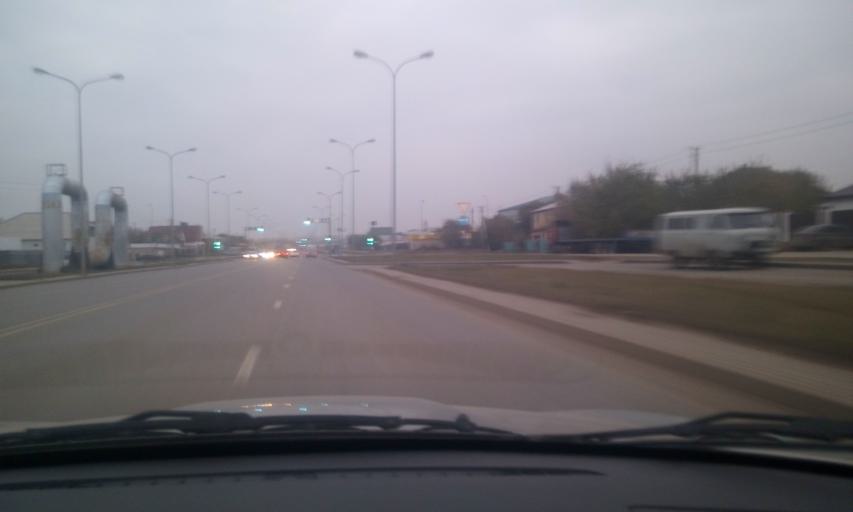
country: KZ
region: Astana Qalasy
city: Astana
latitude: 51.1356
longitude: 71.5107
